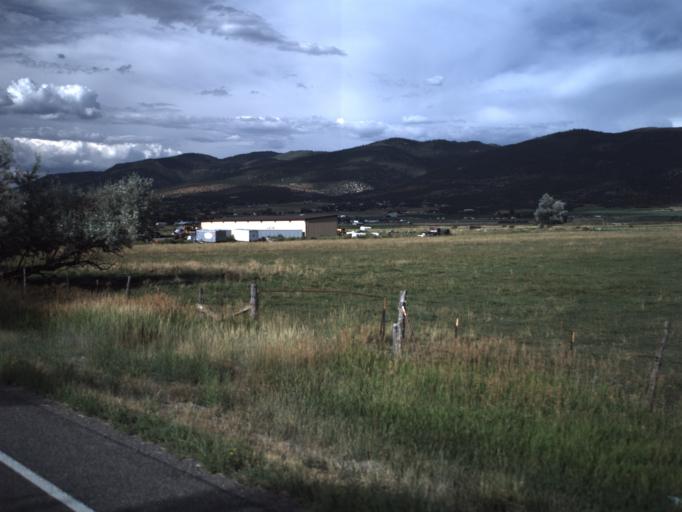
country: US
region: Utah
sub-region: Sanpete County
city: Fairview
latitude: 39.6053
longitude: -111.4447
